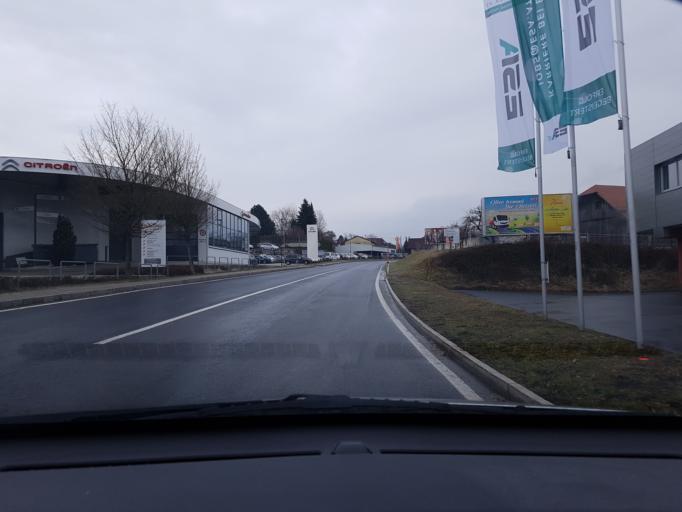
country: AT
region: Upper Austria
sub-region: Steyr Stadt
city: Steyr
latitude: 48.0774
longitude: 14.3805
